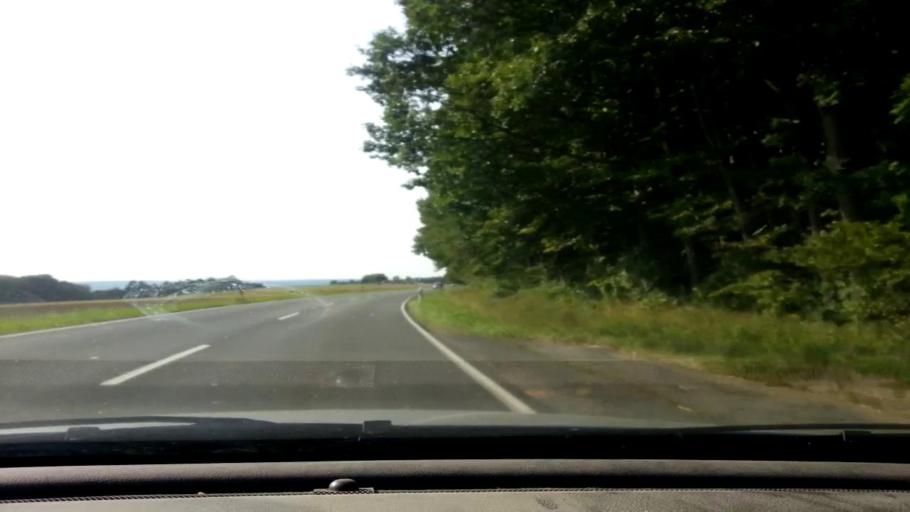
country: DE
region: Bavaria
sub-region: Upper Franconia
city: Zapfendorf
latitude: 50.0019
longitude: 10.9552
